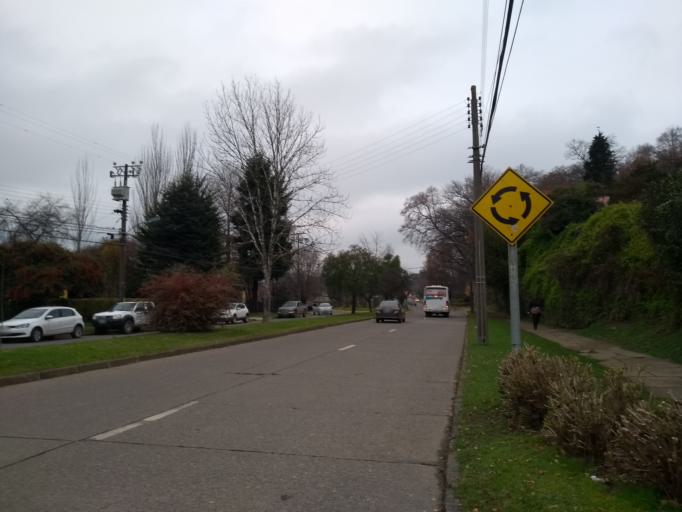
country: CL
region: Los Rios
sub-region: Provincia de Valdivia
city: Valdivia
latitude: -39.8099
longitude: -73.2589
